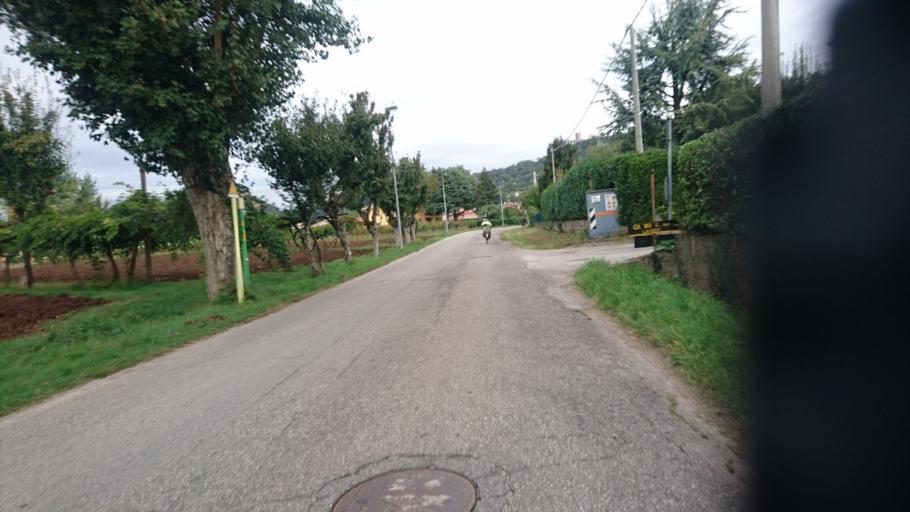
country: IT
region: Veneto
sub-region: Provincia di Vicenza
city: Montecchio Maggiore-Alte Ceccato
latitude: 45.5032
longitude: 11.3983
